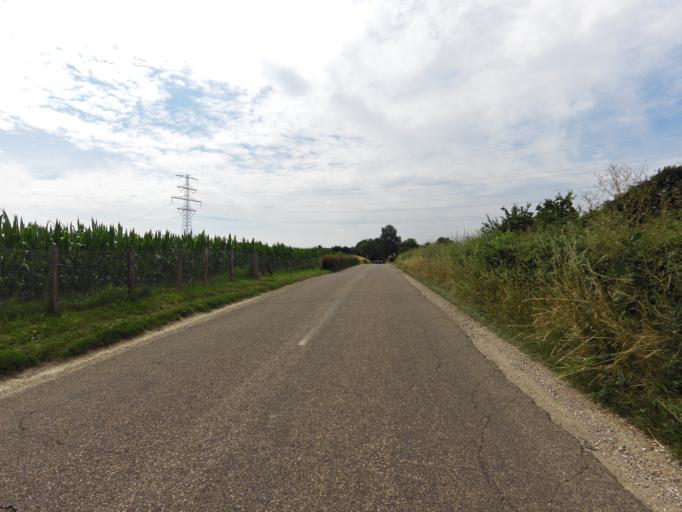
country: NL
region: Limburg
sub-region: Gemeente Voerendaal
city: Klimmen
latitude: 50.8701
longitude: 5.8702
